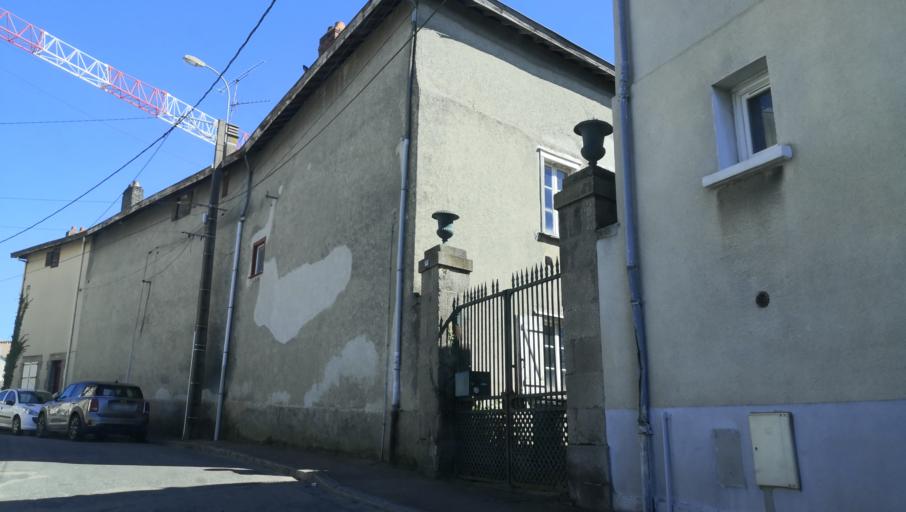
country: FR
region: Limousin
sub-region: Departement de la Haute-Vienne
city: Limoges
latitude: 45.8419
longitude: 1.2630
